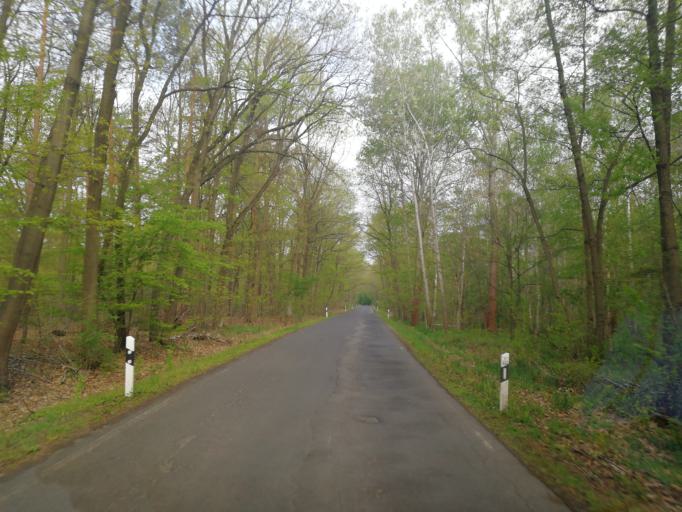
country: DE
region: Brandenburg
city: Herzberg
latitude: 51.6434
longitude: 13.1712
